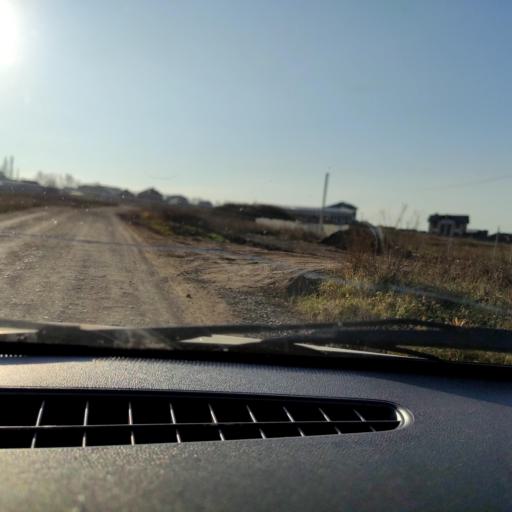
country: RU
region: Bashkortostan
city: Kabakovo
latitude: 54.6355
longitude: 56.0743
